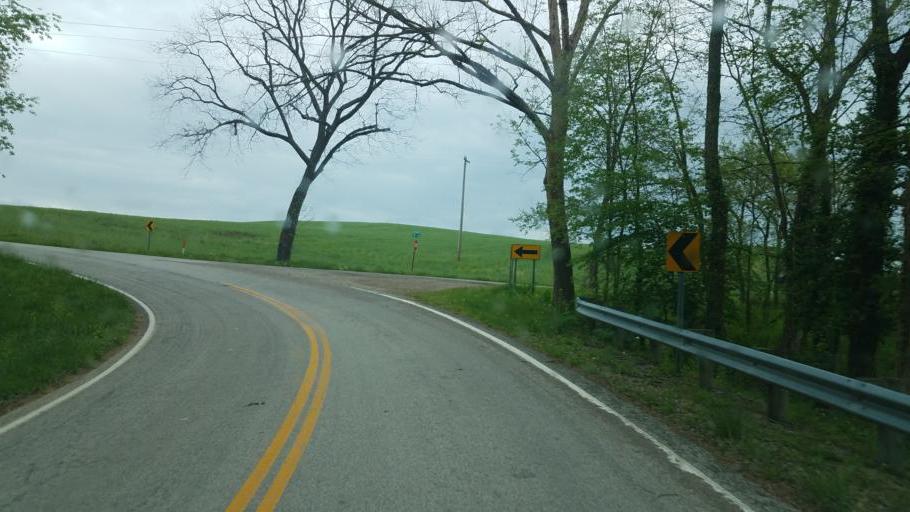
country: US
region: Ohio
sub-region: Ashland County
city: Loudonville
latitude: 40.6420
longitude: -82.3219
